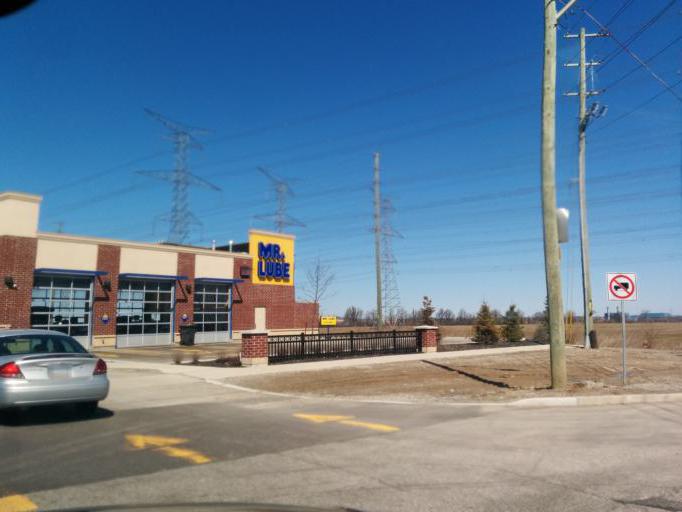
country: CA
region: Ontario
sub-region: Halton
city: Milton
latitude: 43.5388
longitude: -79.8554
